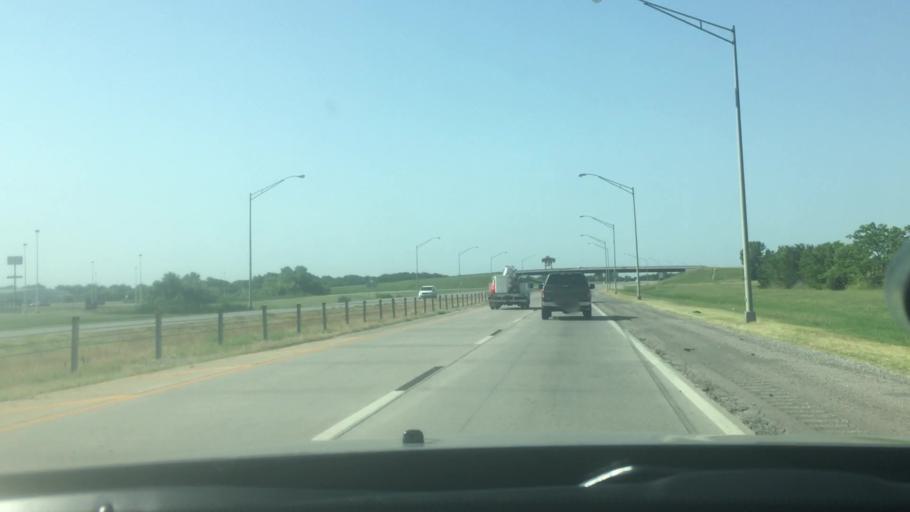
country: US
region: Oklahoma
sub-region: Bryan County
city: Calera
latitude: 33.9510
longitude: -96.4168
